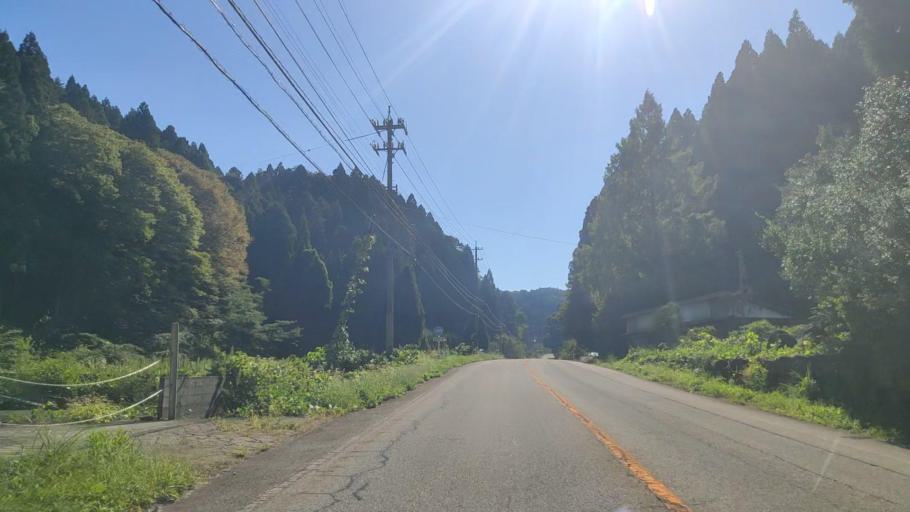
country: JP
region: Ishikawa
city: Nanao
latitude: 37.3248
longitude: 137.1930
